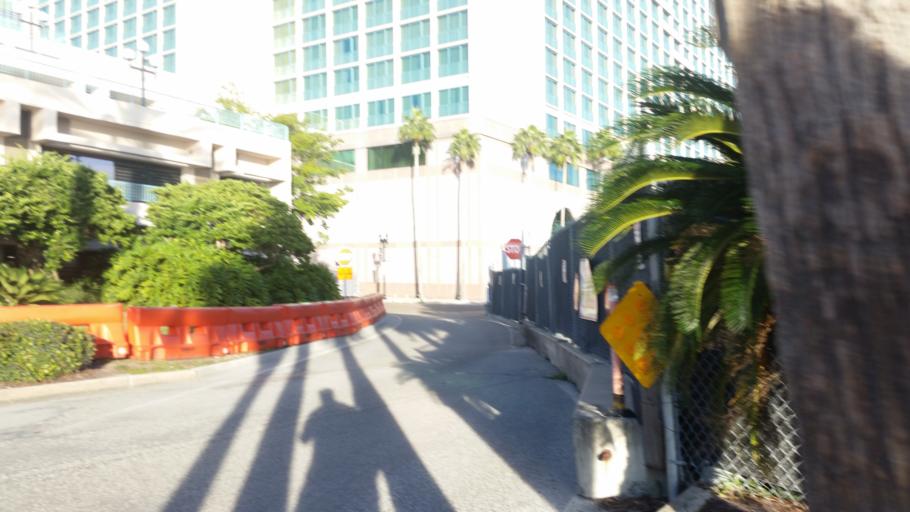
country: US
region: Florida
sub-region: Duval County
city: Jacksonville
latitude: 30.3238
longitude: -81.6565
